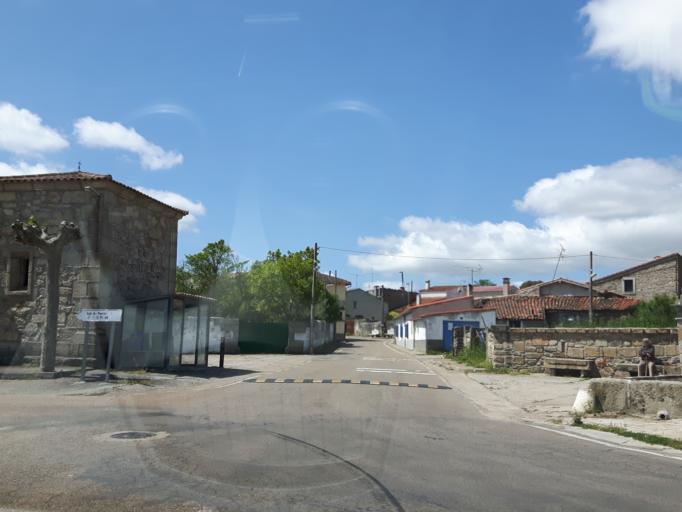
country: ES
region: Castille and Leon
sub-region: Provincia de Salamanca
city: Aldea del Obispo
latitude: 40.7096
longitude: -6.7940
